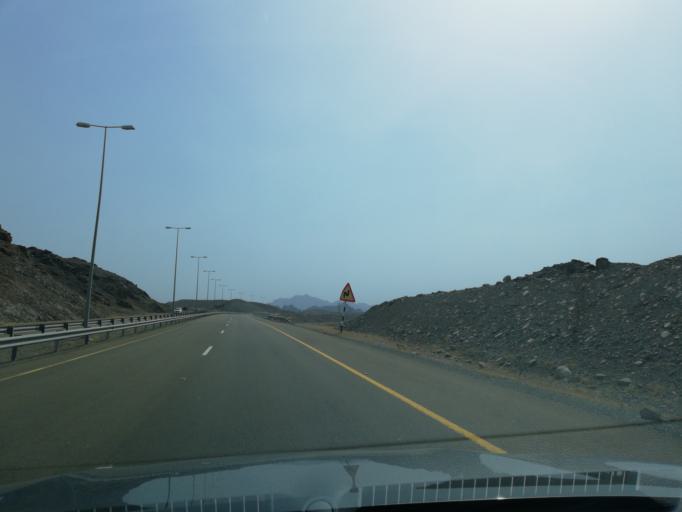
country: OM
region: Al Batinah
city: Al Liwa'
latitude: 24.2844
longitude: 56.4117
